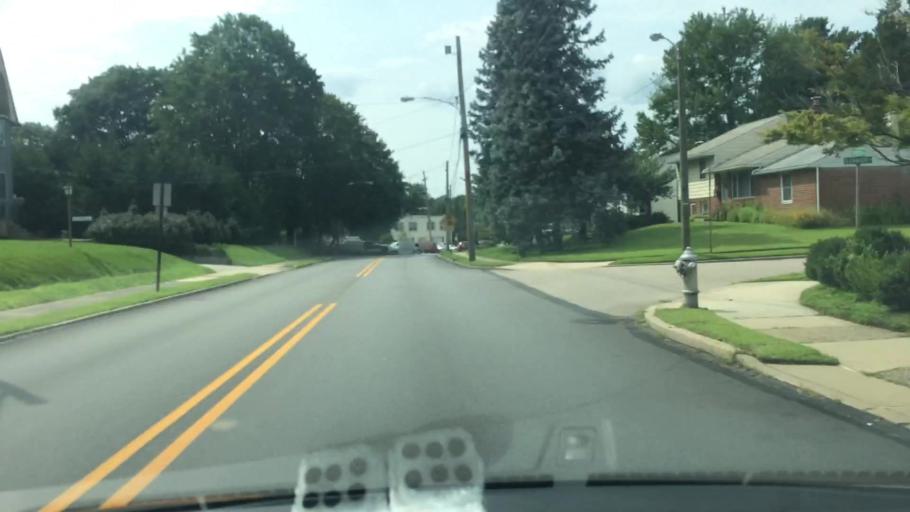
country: US
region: Pennsylvania
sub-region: Delaware County
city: Aldan
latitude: 39.9255
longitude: -75.2875
